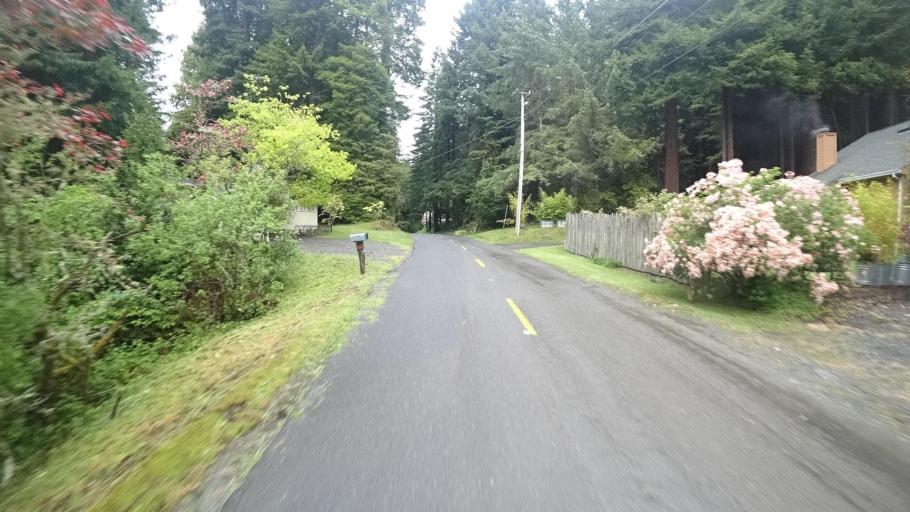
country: US
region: California
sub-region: Humboldt County
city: Bayside
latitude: 40.8233
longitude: -124.0337
